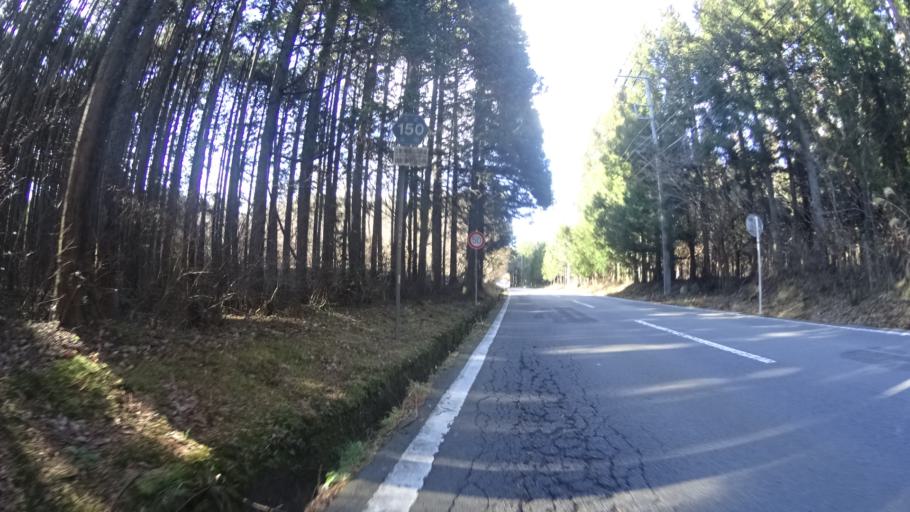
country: JP
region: Shizuoka
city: Gotemba
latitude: 35.3436
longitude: 138.9015
